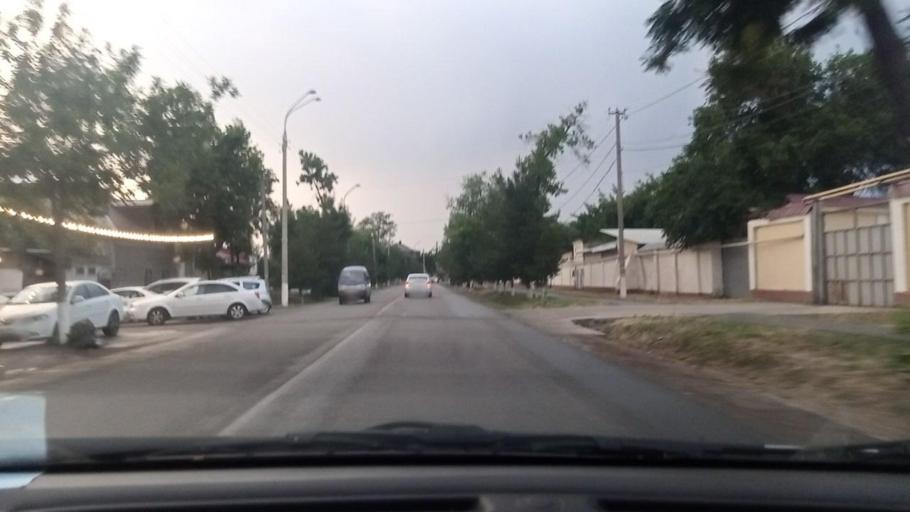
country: UZ
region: Toshkent Shahri
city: Tashkent
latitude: 41.2830
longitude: 69.2846
